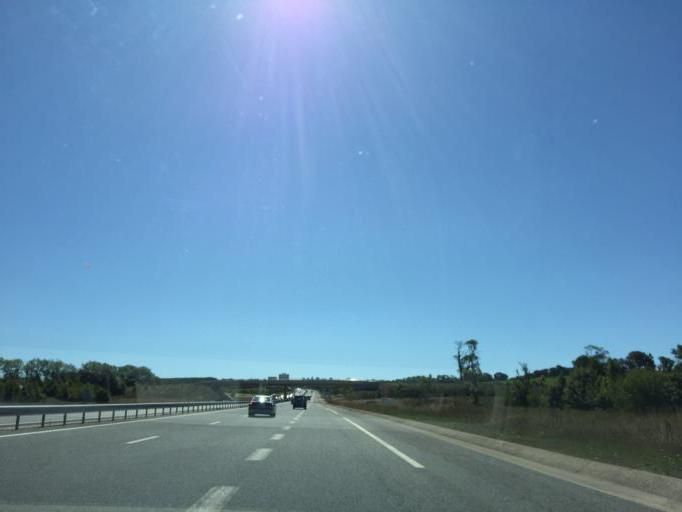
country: FR
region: Midi-Pyrenees
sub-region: Departement de l'Aveyron
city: La Cavalerie
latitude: 44.0090
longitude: 3.1440
